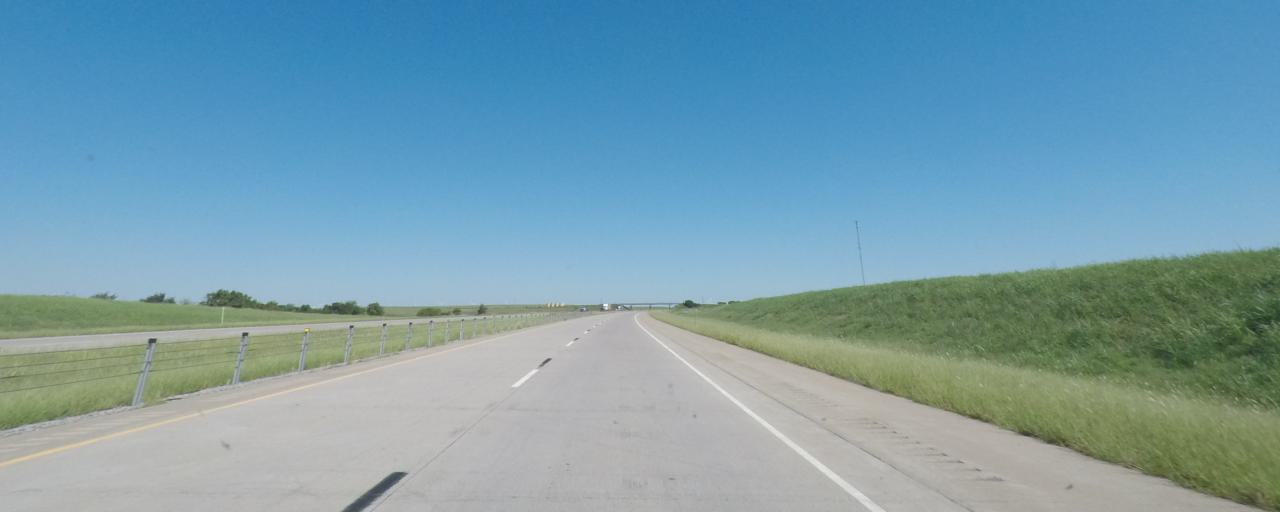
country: US
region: Oklahoma
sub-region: Kay County
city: Tonkawa
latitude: 36.5013
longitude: -97.3346
